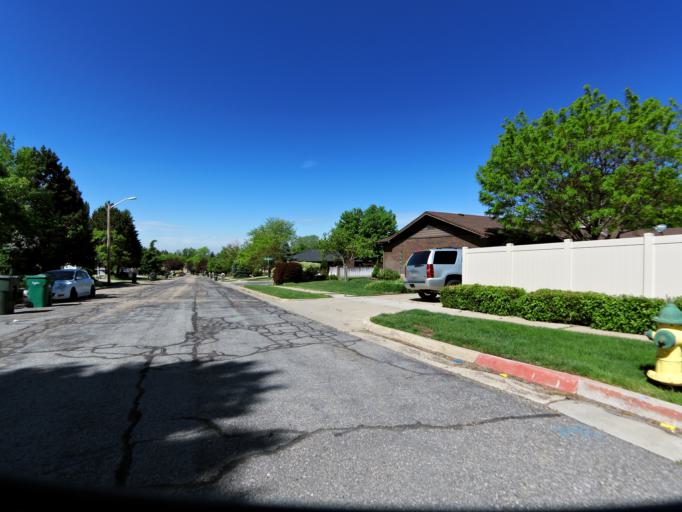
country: US
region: Utah
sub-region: Weber County
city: Uintah
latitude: 41.1705
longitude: -111.9300
